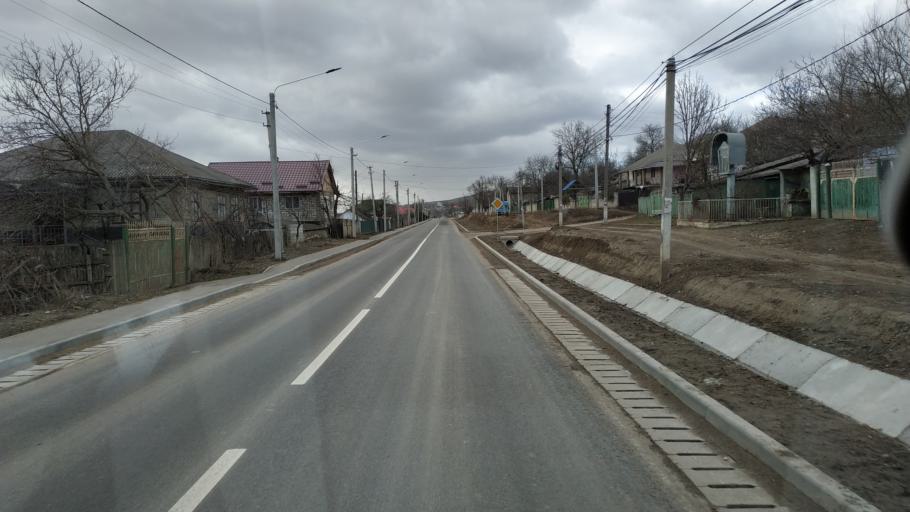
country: MD
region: Calarasi
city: Calarasi
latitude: 47.2834
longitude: 28.2037
